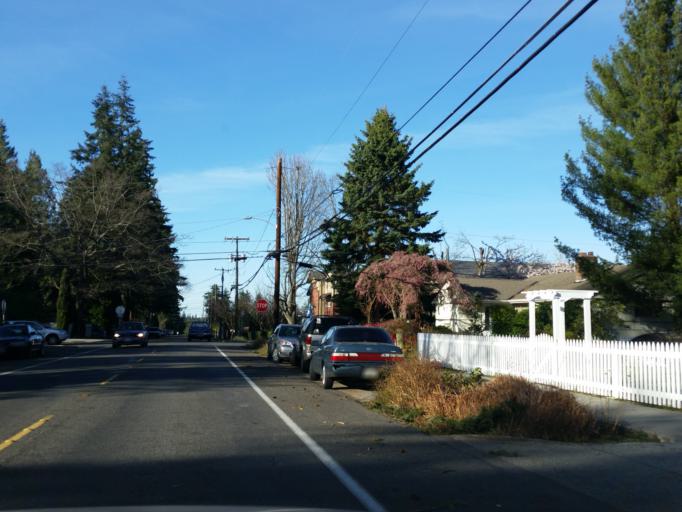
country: US
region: Washington
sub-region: King County
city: Shoreline
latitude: 47.7673
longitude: -122.3405
